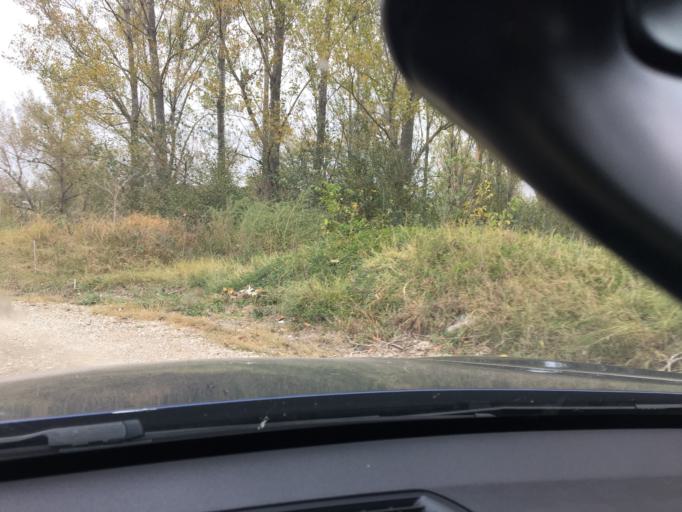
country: BG
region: Pleven
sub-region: Obshtina Dolna Mitropoliya
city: Dolna Mitropoliya
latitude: 43.4434
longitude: 24.5552
